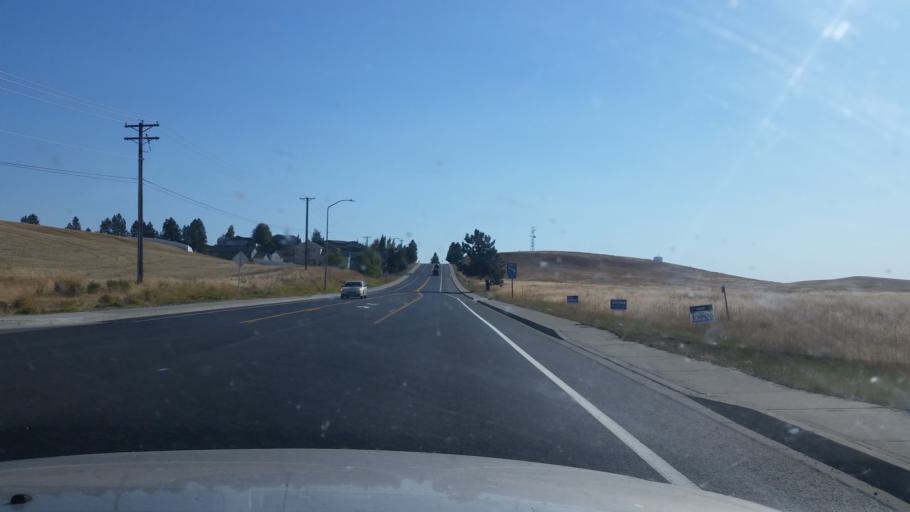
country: US
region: Washington
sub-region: Spokane County
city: Cheney
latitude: 47.5038
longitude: -117.5863
